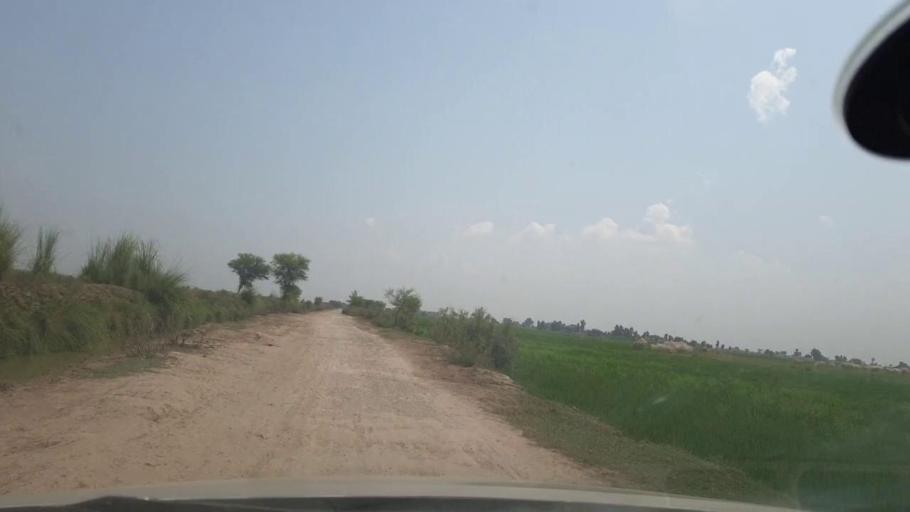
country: PK
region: Sindh
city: Jacobabad
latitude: 28.1358
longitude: 68.3769
